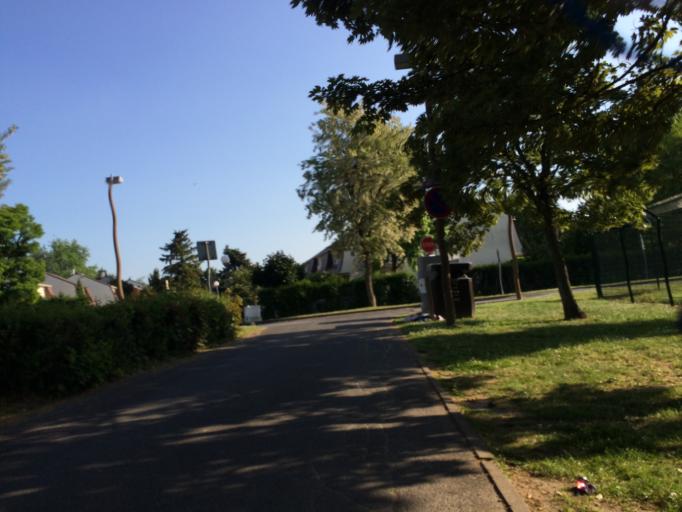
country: FR
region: Ile-de-France
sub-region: Departement de l'Essonne
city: Bondoufle
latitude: 48.6151
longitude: 2.3875
